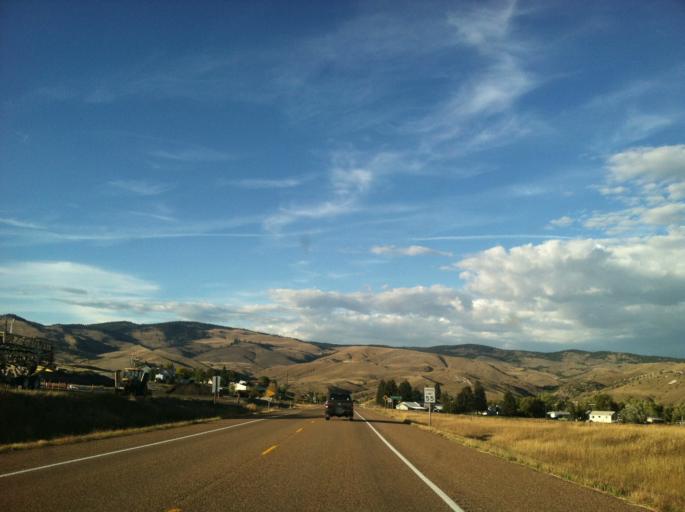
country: US
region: Montana
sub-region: Granite County
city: Philipsburg
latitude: 46.6571
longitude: -113.1590
